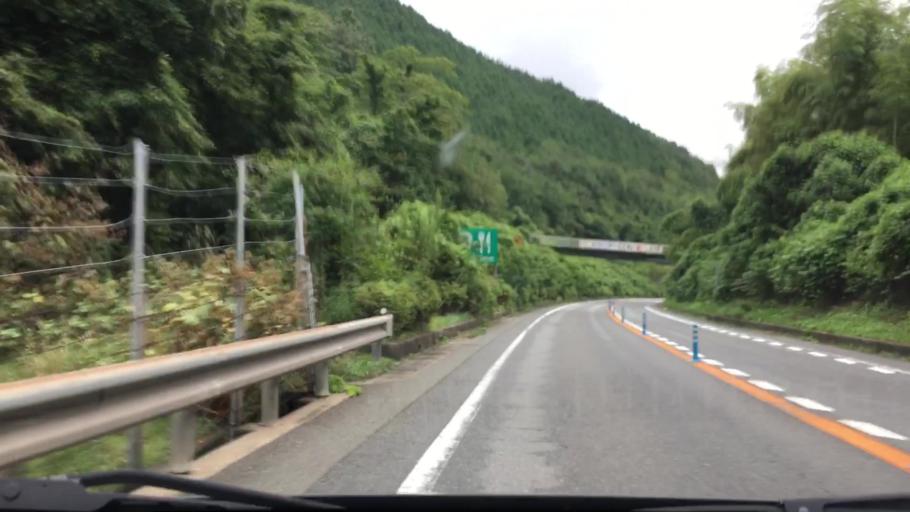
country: JP
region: Hyogo
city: Nishiwaki
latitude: 35.0400
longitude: 134.7694
